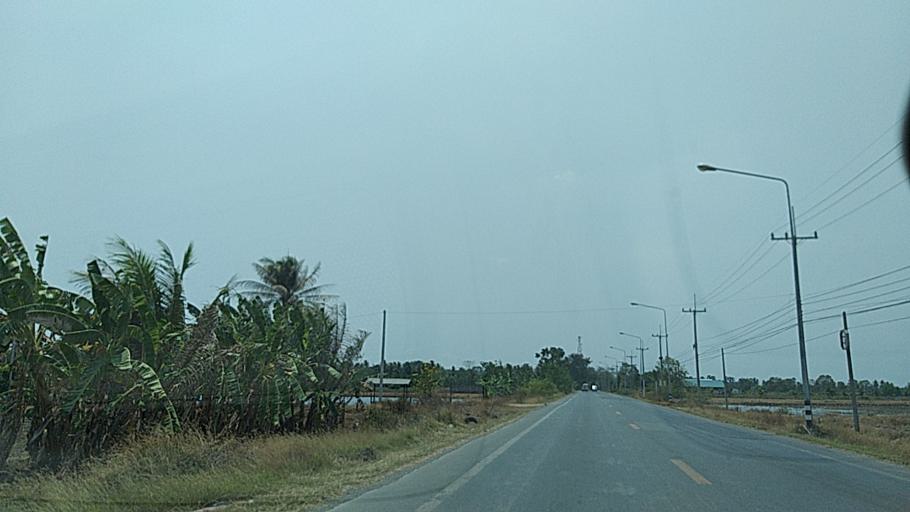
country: TH
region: Chachoengsao
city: Bang Nam Priao
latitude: 13.8873
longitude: 100.9699
